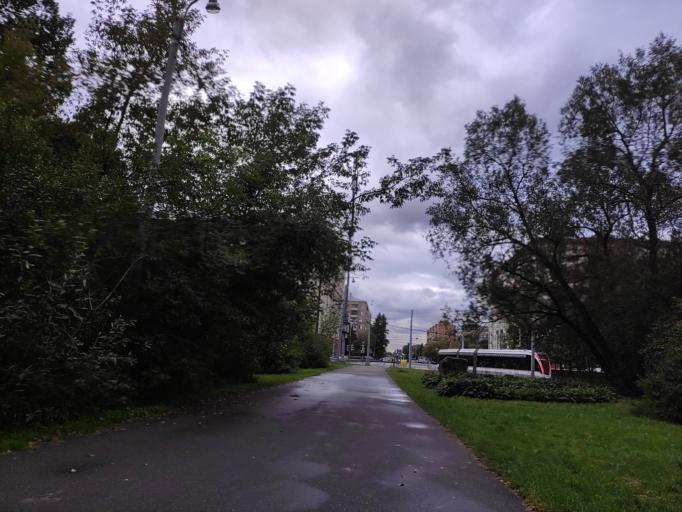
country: RU
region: Moskovskaya
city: Izmaylovo
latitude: 55.7659
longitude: 37.7838
